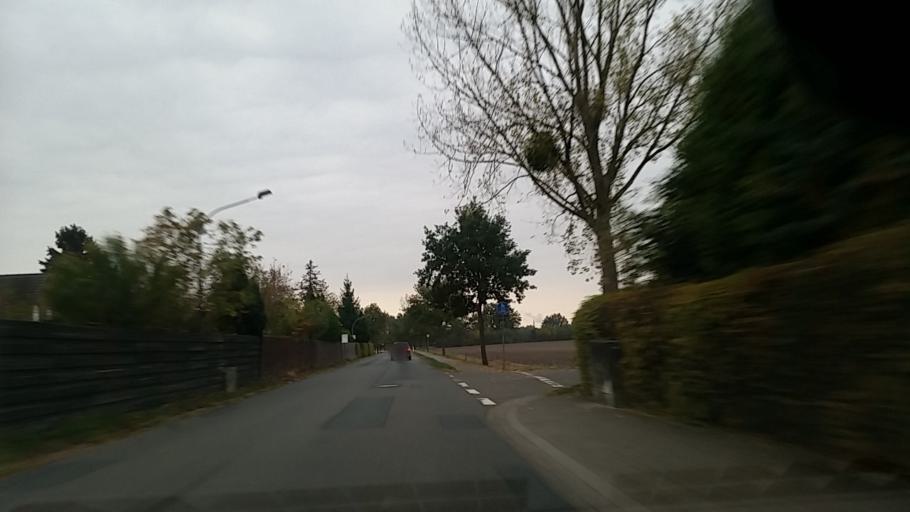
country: DE
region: Lower Saxony
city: Jembke
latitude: 52.4934
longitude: 10.7609
